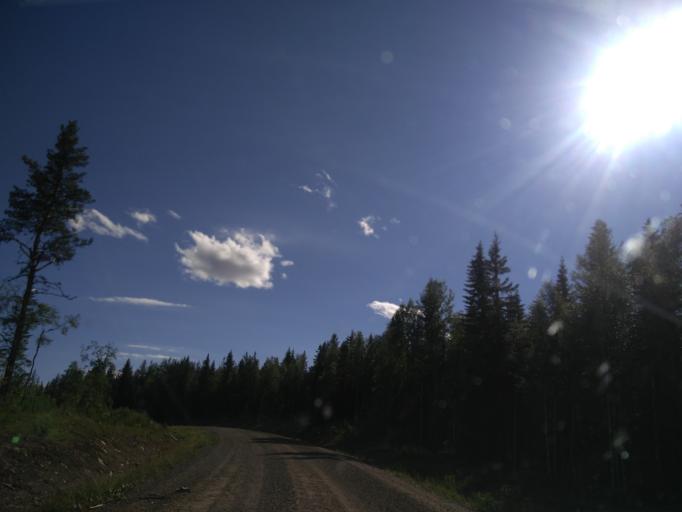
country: SE
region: Vaesternorrland
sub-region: Ange Kommun
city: Fransta
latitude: 62.2785
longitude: 16.3130
